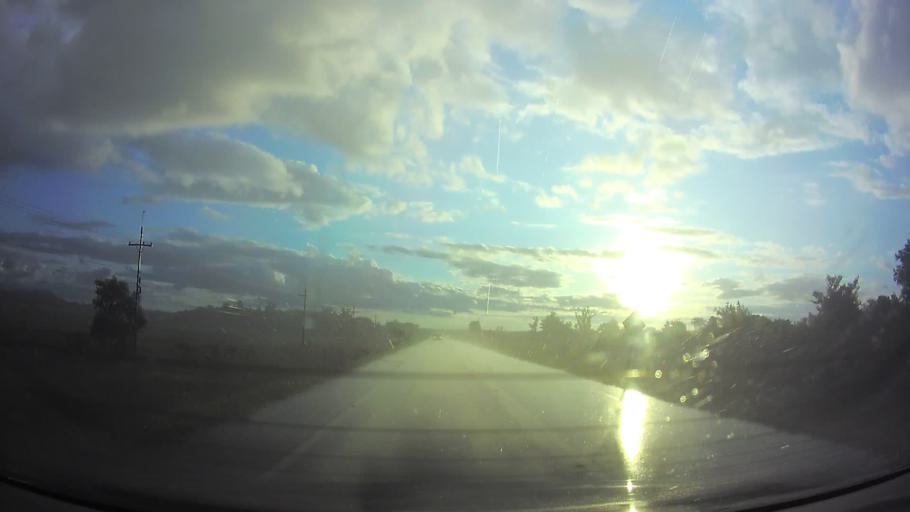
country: PY
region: Paraguari
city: Paraguari
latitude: -25.7067
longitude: -57.1849
